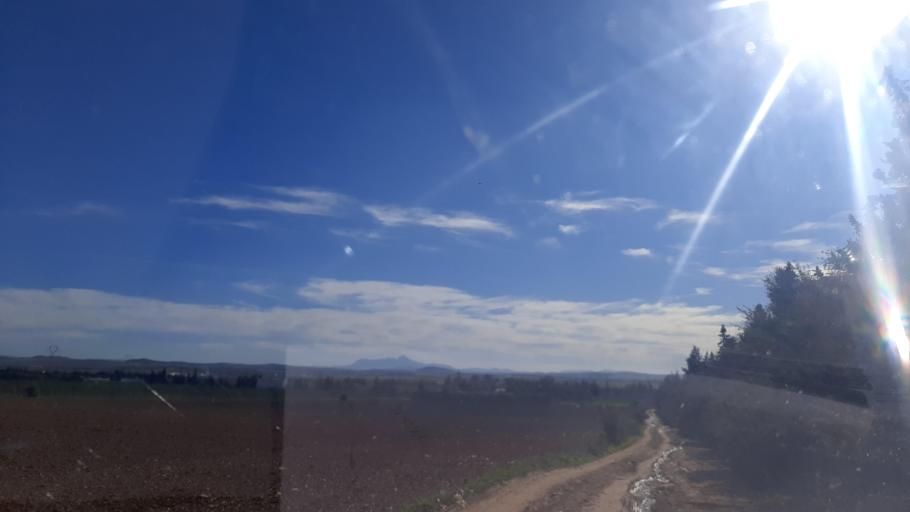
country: TN
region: Tunis
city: Oued Lill
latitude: 36.7612
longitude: 9.9821
